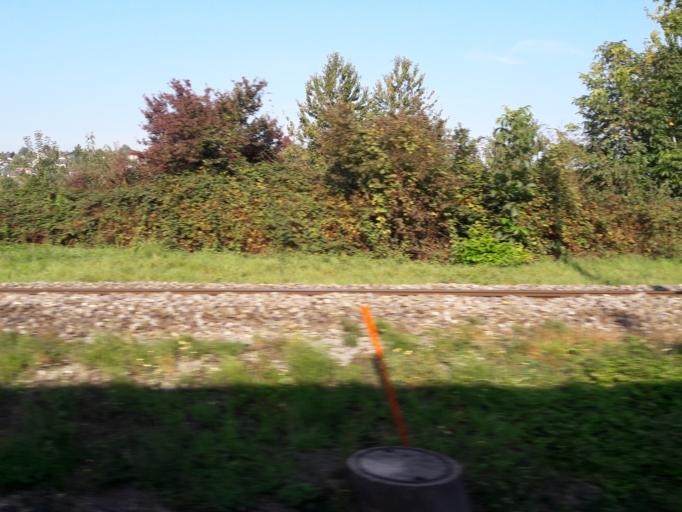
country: CH
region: Vaud
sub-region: Ouest Lausannois District
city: Ecublens
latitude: 46.5373
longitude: 6.5550
